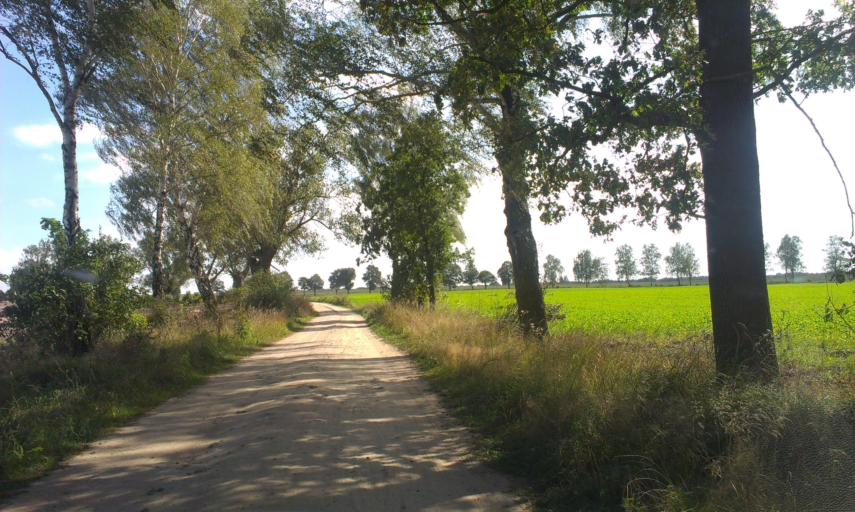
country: PL
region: Greater Poland Voivodeship
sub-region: Powiat pilski
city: Lobzenica
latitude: 53.2861
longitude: 17.1710
